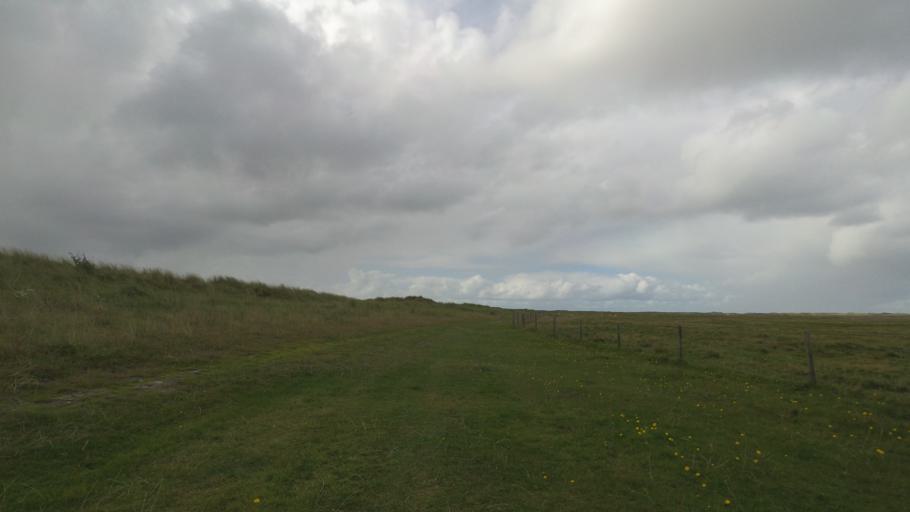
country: NL
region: Friesland
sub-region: Gemeente Ameland
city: Nes
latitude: 53.4511
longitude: 5.8539
